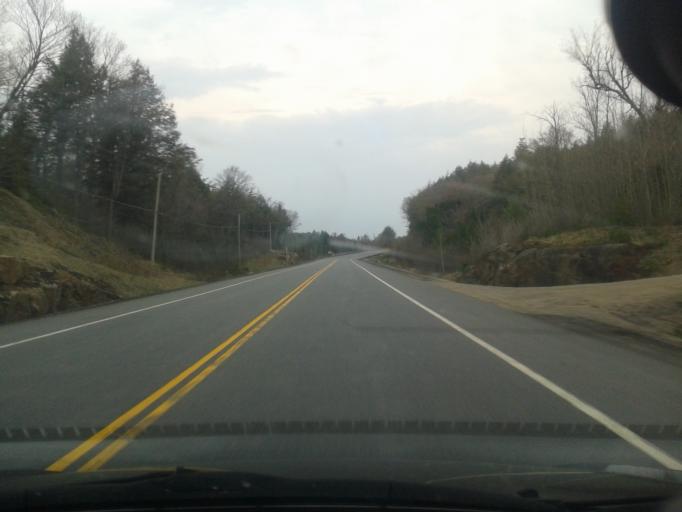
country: CA
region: Ontario
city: Huntsville
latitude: 45.5086
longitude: -78.7247
